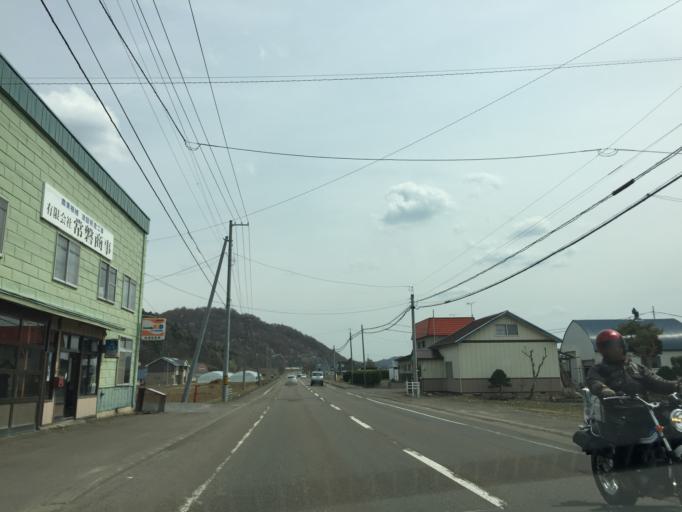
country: JP
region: Hokkaido
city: Ashibetsu
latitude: 43.5431
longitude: 142.1584
